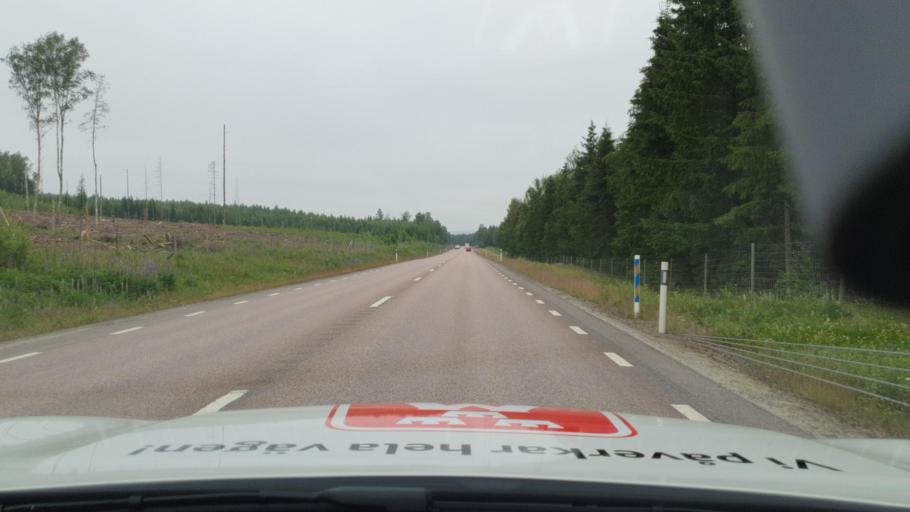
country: SE
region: Vaermland
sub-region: Sunne Kommun
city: Sunne
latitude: 59.7552
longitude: 13.1174
